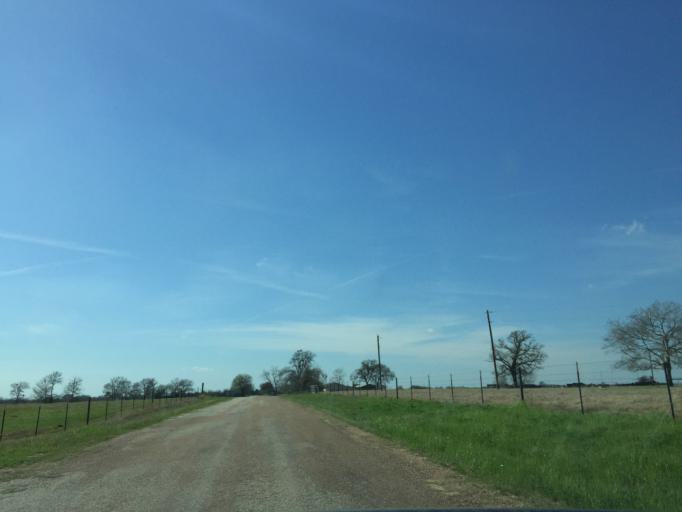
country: US
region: Texas
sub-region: Milam County
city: Thorndale
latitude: 30.5776
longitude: -97.1748
